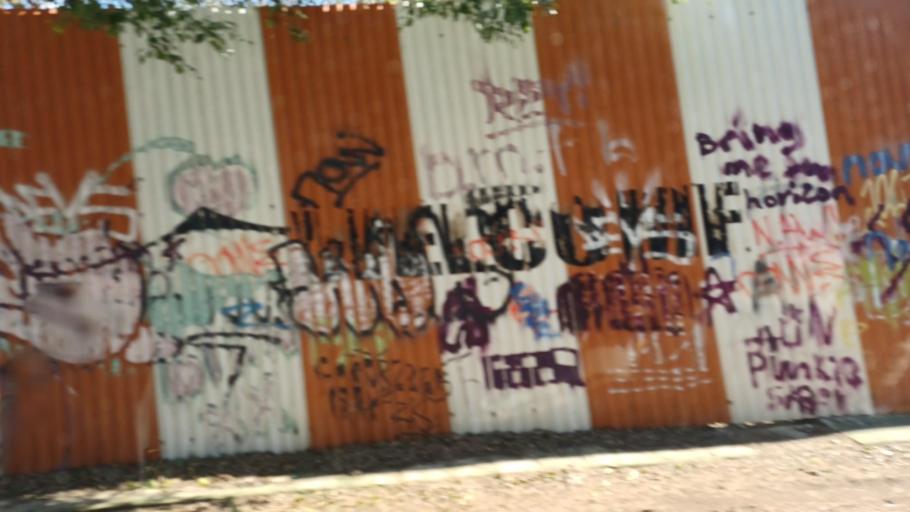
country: CY
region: Pafos
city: Paphos
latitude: 34.7497
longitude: 32.4376
